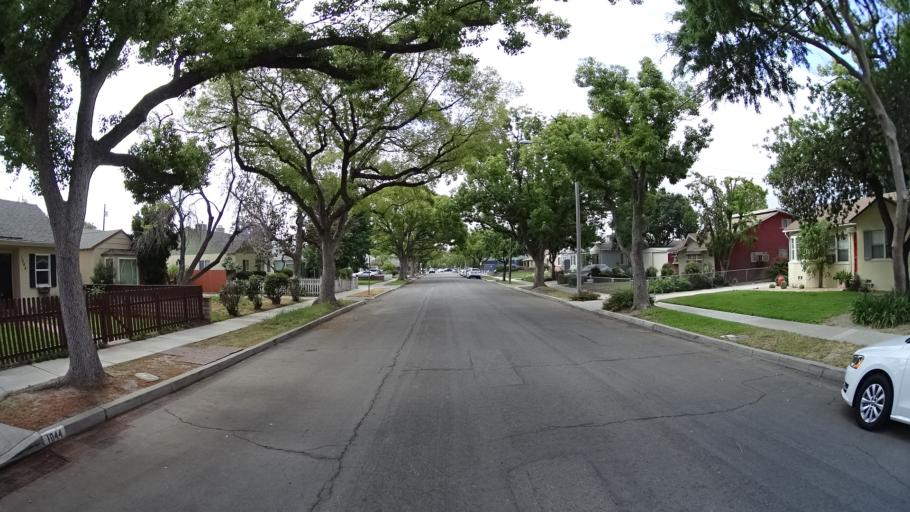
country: US
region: California
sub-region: Los Angeles County
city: North Hollywood
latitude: 34.1671
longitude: -118.3548
